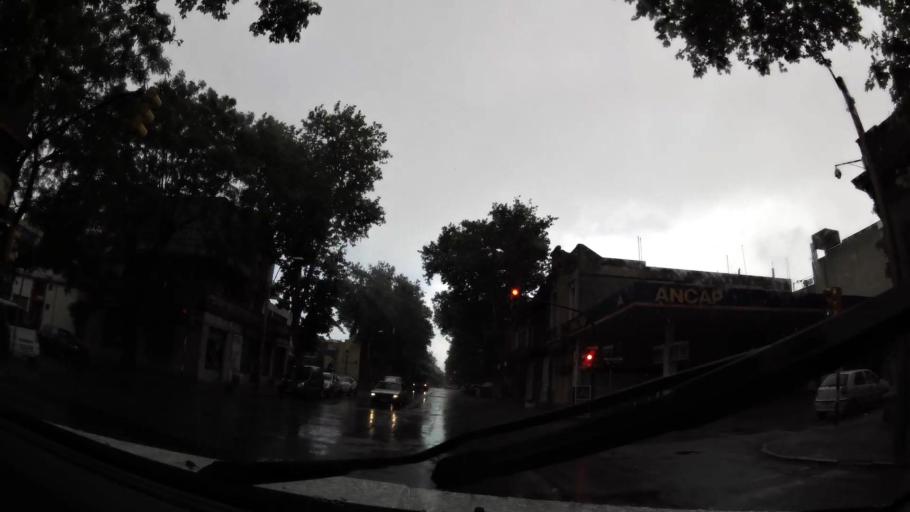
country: UY
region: Montevideo
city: Montevideo
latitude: -34.8870
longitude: -56.1852
